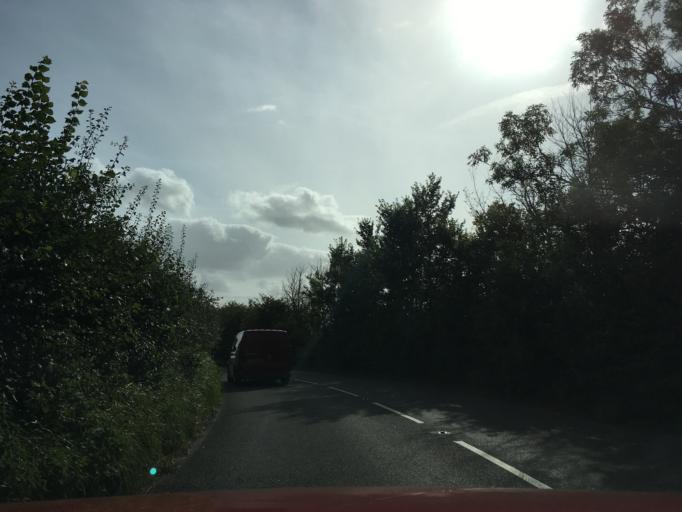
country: GB
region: England
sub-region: South Gloucestershire
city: Charfield
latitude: 51.6333
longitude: -2.3797
